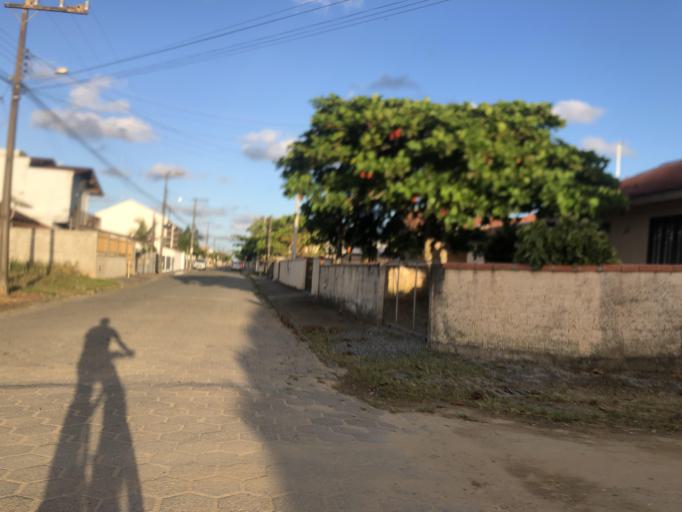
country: BR
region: Santa Catarina
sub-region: Sao Francisco Do Sul
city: Sao Francisco do Sul
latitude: -26.2196
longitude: -48.5297
